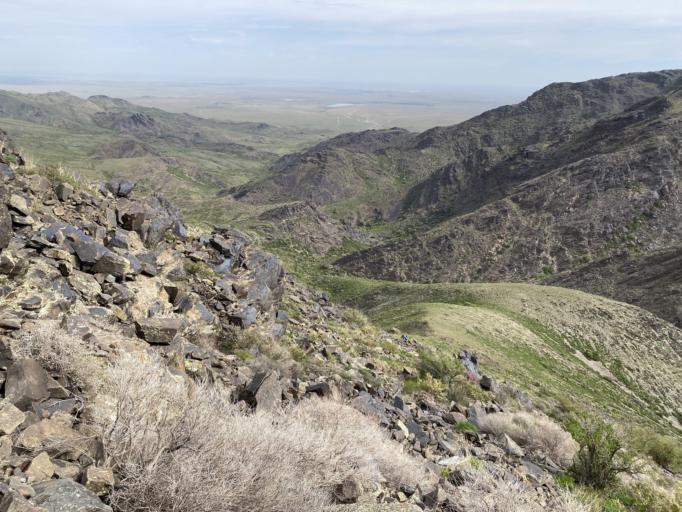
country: KZ
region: Ongtustik Qazaqstan
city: Kentau
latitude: 43.8413
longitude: 68.5001
